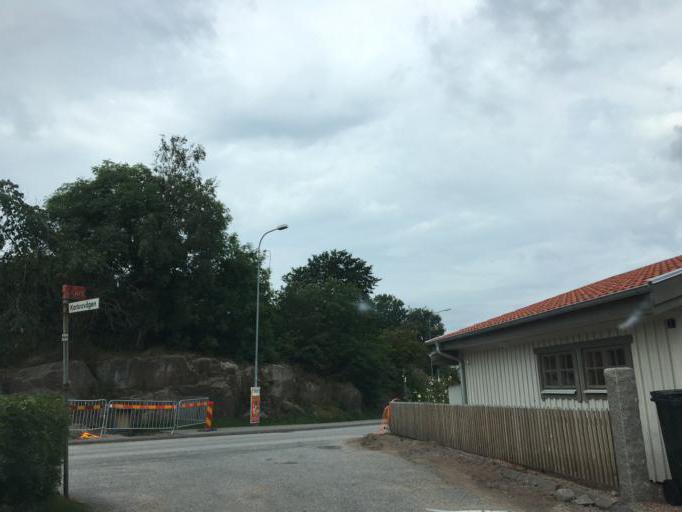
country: SE
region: Vaestra Goetaland
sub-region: Sotenas Kommun
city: Hunnebostrand
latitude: 58.4406
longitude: 11.3082
